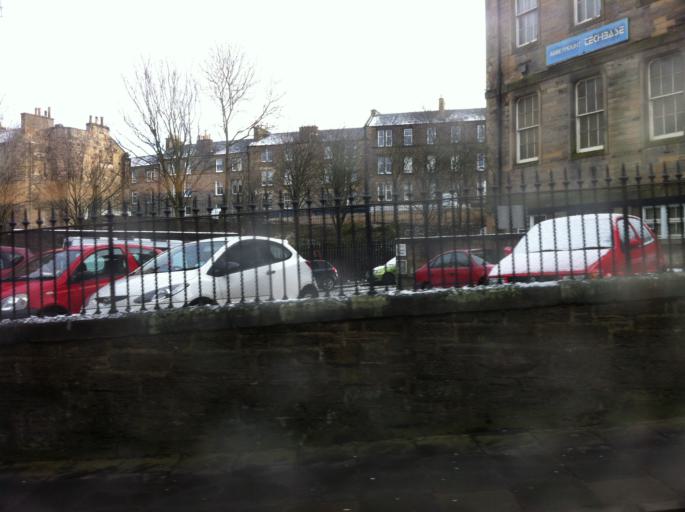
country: GB
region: Scotland
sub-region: West Lothian
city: Seafield
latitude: 55.9572
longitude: -3.1725
